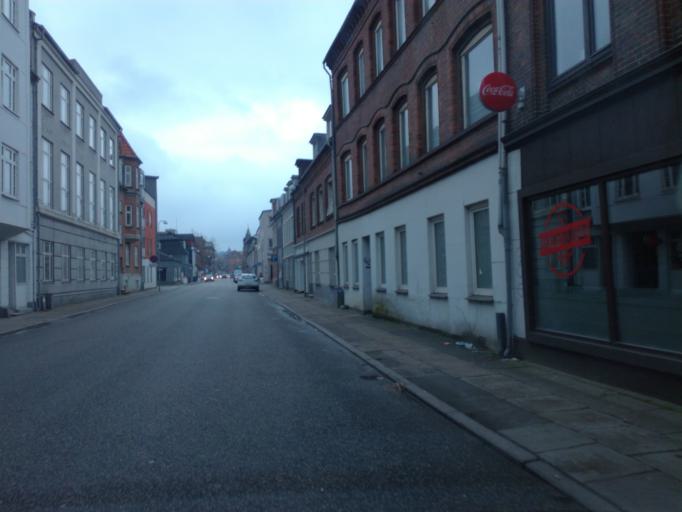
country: DK
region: South Denmark
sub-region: Vejle Kommune
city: Vejle
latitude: 55.7132
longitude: 9.5334
